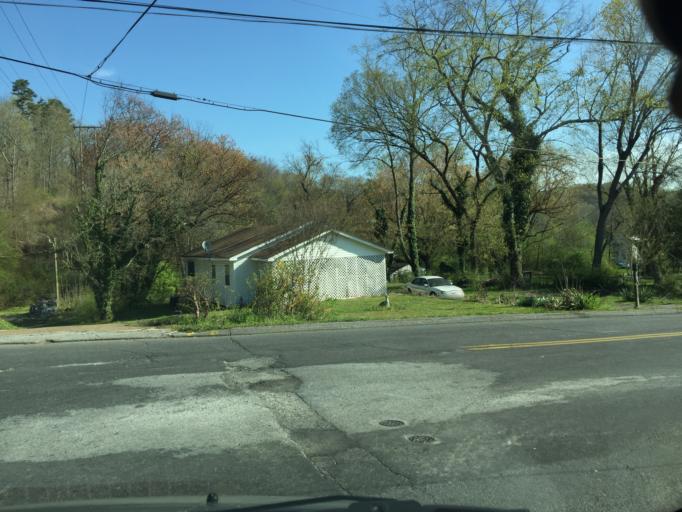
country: US
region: Tennessee
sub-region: Hamilton County
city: East Chattanooga
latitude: 35.0677
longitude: -85.2282
